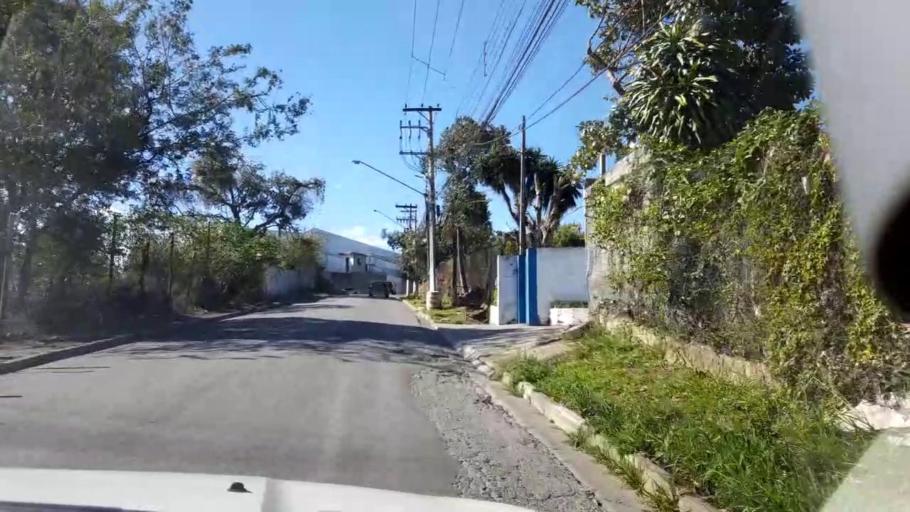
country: BR
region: Sao Paulo
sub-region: Ferraz De Vasconcelos
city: Ferraz de Vasconcelos
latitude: -23.5304
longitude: -46.3911
